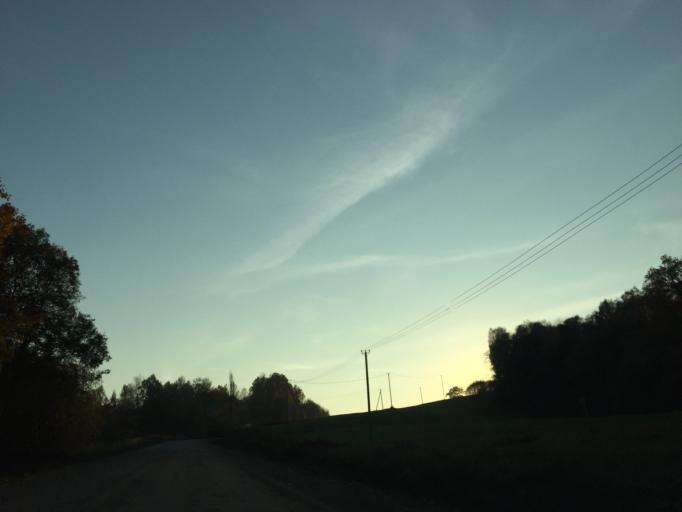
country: LV
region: Vainode
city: Vainode
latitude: 56.5028
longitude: 21.8101
